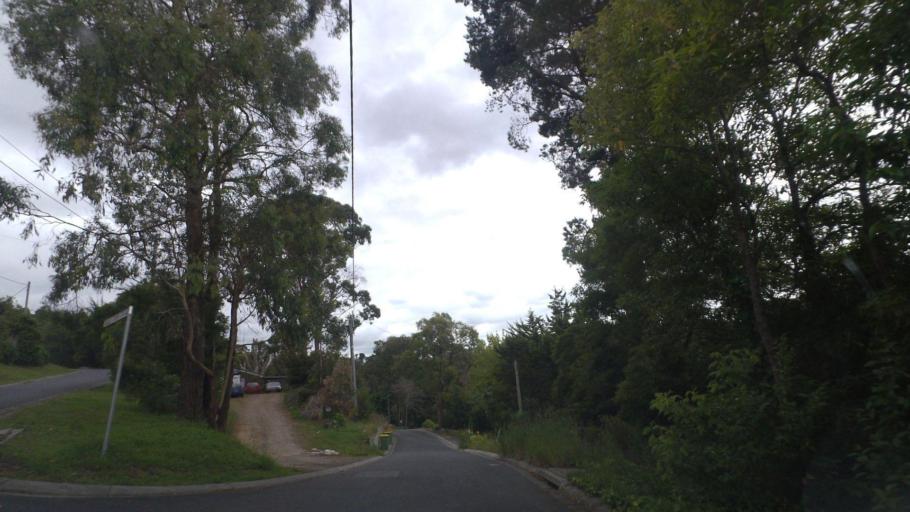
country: AU
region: Victoria
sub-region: Yarra Ranges
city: Mount Evelyn
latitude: -37.7899
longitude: 145.3736
